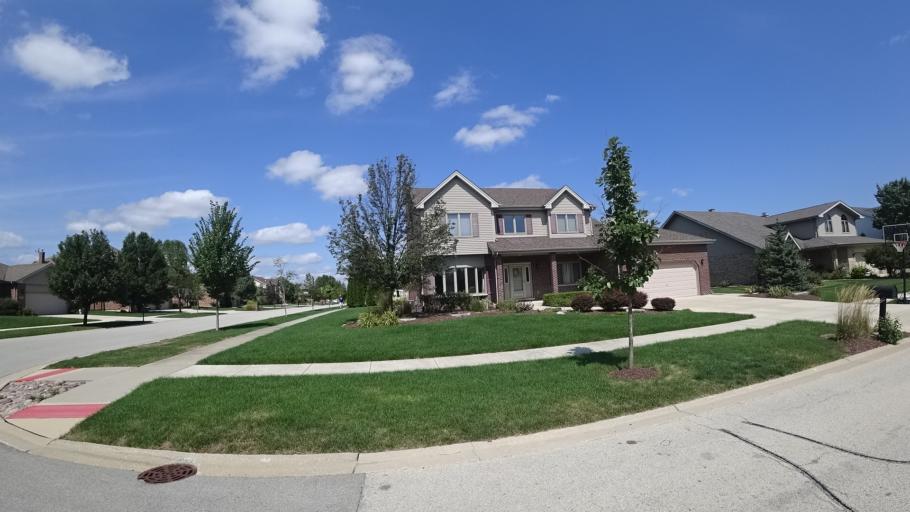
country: US
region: Illinois
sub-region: Cook County
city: Orland Hills
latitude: 41.5659
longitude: -87.8337
